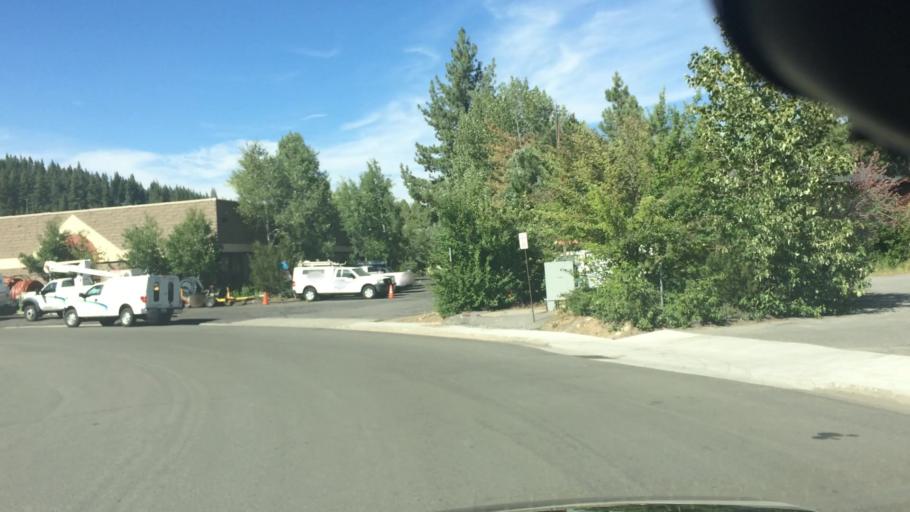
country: US
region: California
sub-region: Nevada County
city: Truckee
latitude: 39.3222
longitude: -120.1931
